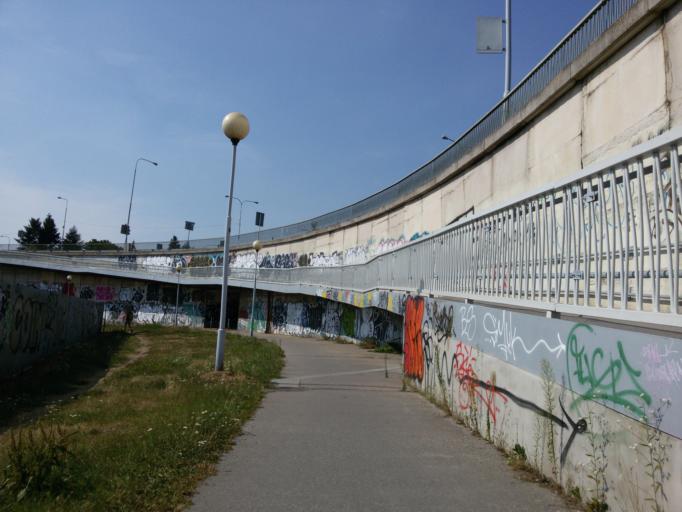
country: CZ
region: South Moravian
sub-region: Mesto Brno
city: Brno
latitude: 49.2266
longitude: 16.6010
